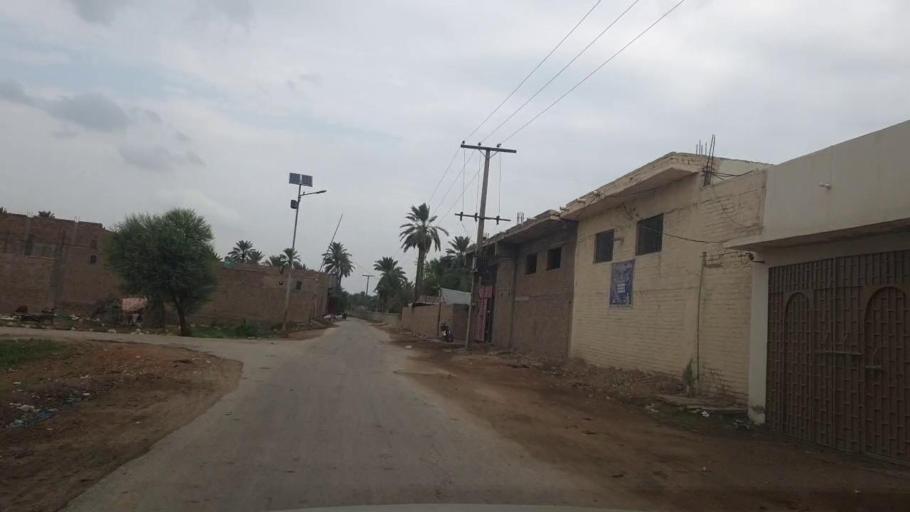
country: PK
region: Sindh
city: Khairpur
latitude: 27.5428
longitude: 68.7551
